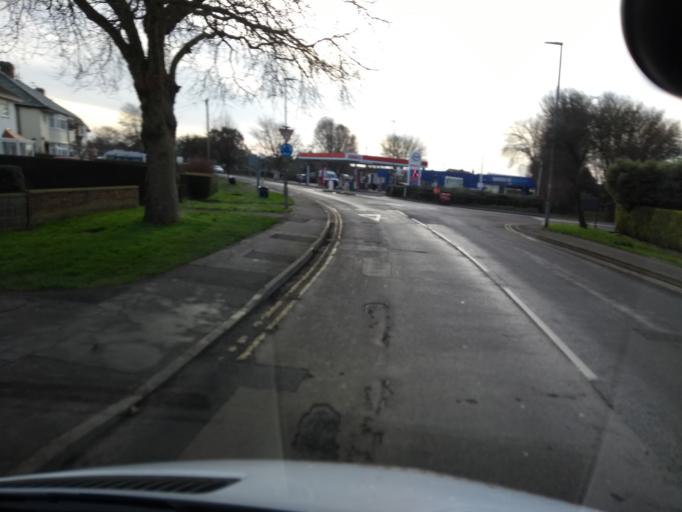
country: GB
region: England
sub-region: Somerset
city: Highbridge
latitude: 51.2276
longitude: -2.9877
